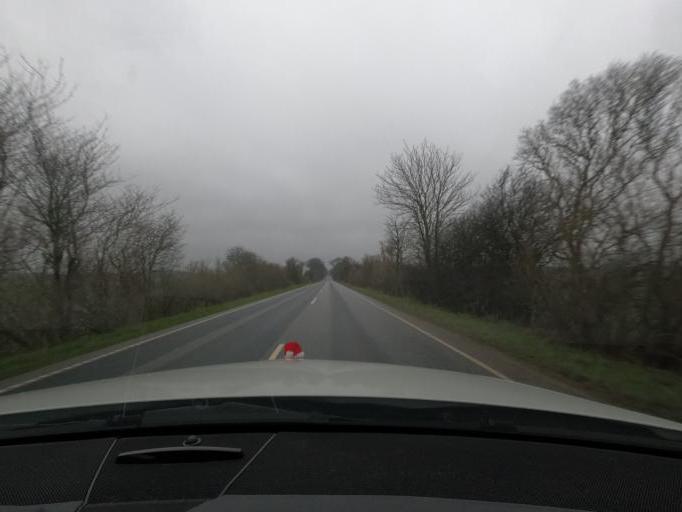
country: DK
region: South Denmark
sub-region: Haderslev Kommune
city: Starup
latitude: 55.2144
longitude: 9.5958
